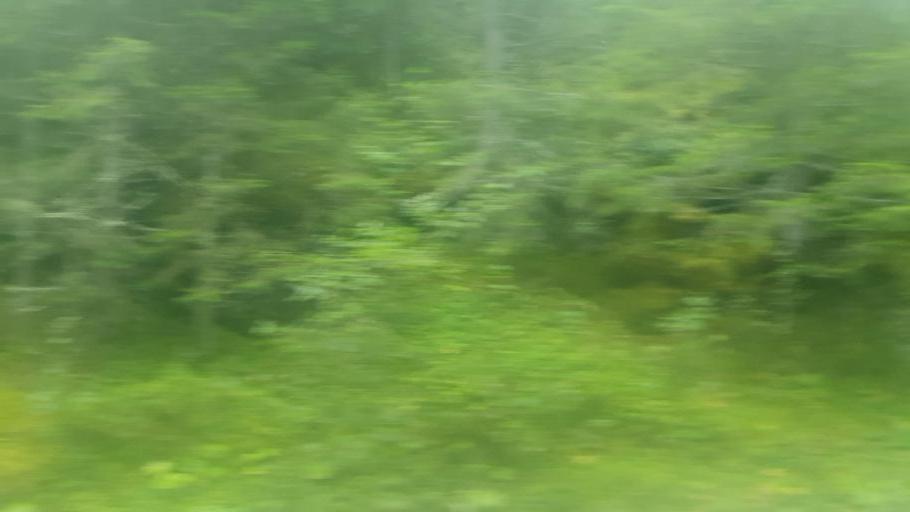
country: NO
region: Nord-Trondelag
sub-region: Levanger
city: Skogn
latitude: 63.6183
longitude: 11.2184
